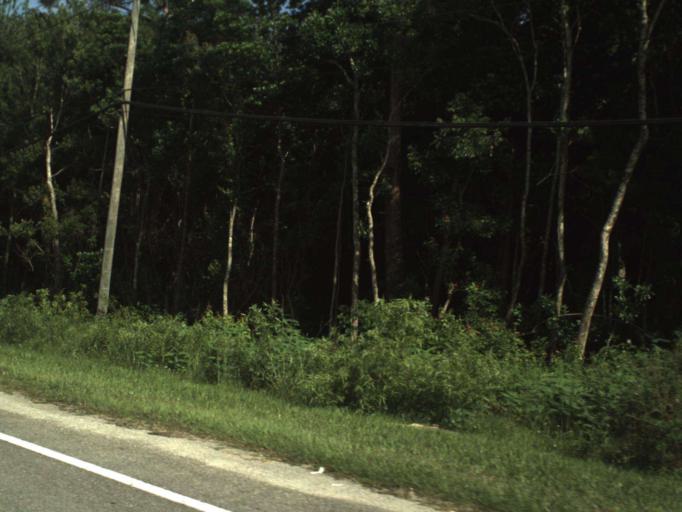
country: US
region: Florida
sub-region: Volusia County
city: DeLand
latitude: 29.0250
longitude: -81.2639
